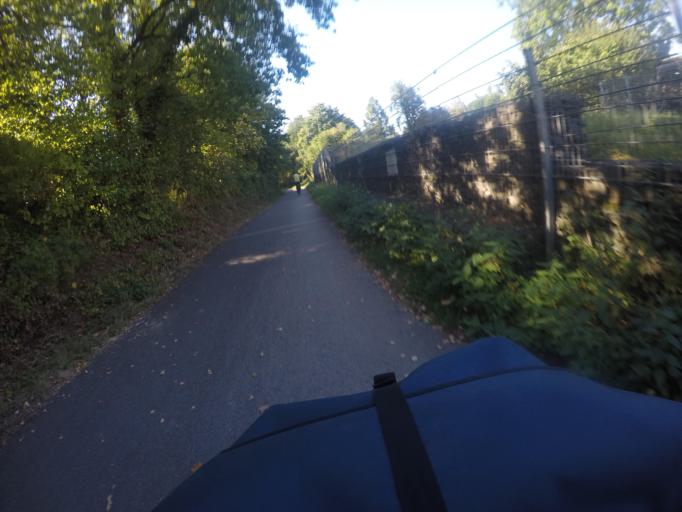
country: DE
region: North Rhine-Westphalia
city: Haan
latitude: 51.2136
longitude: 7.0415
